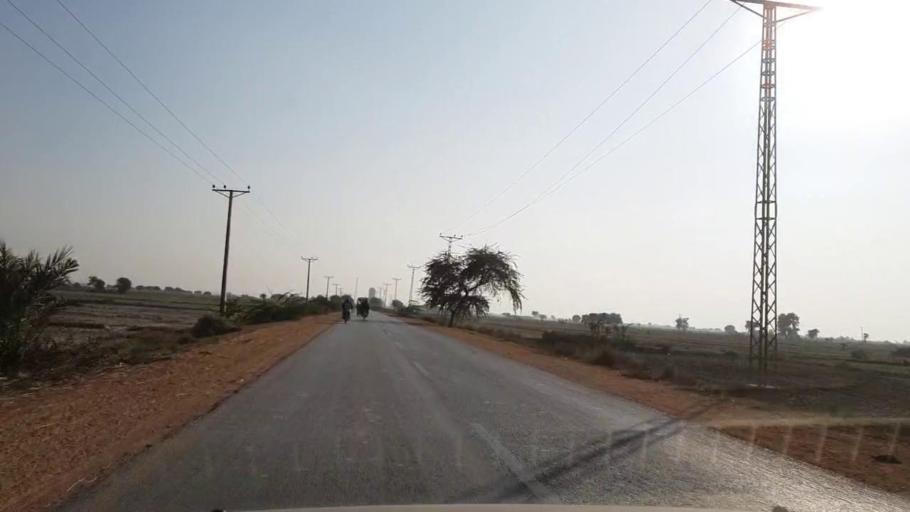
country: PK
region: Sindh
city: Bulri
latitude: 24.8412
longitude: 68.3250
